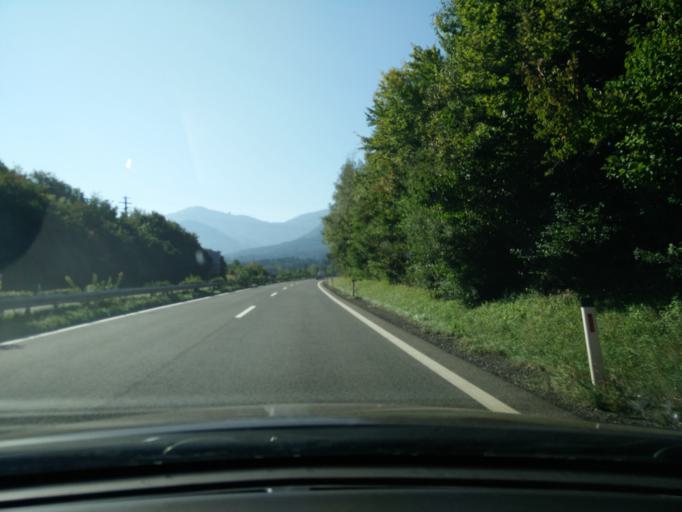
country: AT
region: Carinthia
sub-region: Politischer Bezirk Villach Land
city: Rosegg
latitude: 46.5702
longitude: 14.0058
